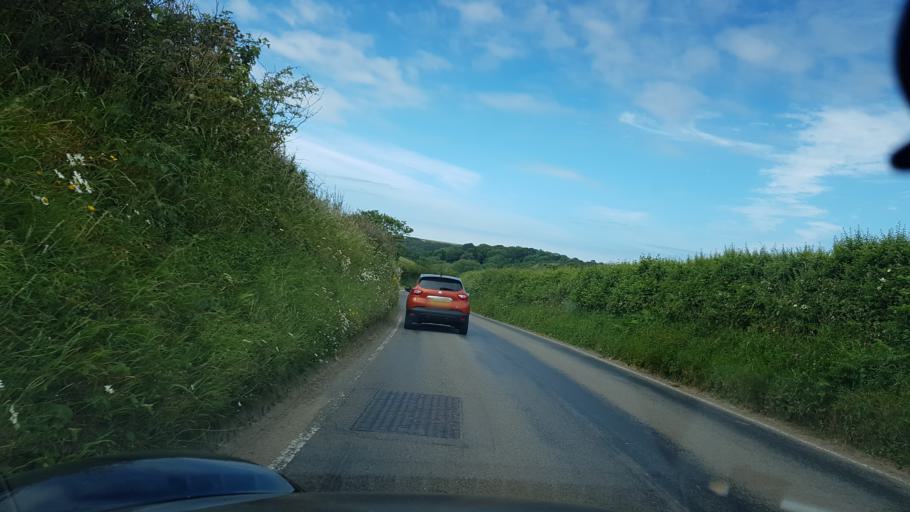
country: GB
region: Wales
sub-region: Pembrokeshire
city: Herbrandston
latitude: 51.7663
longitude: -5.0723
